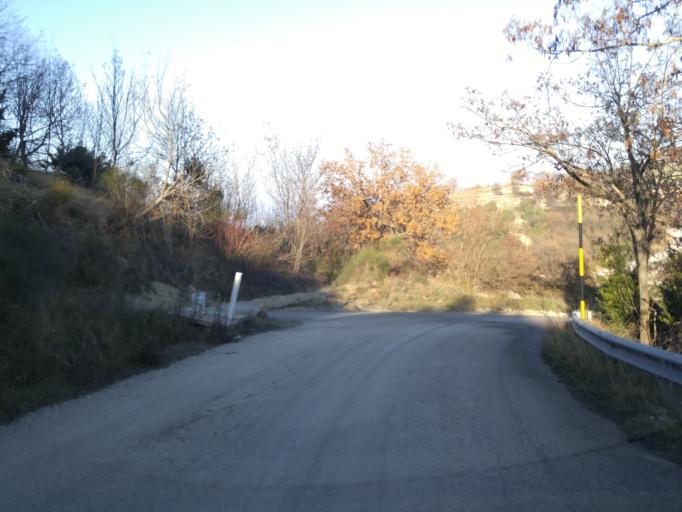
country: IT
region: The Marches
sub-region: Provincia di Pesaro e Urbino
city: Mombaroccio
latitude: 43.7722
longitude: 12.8259
